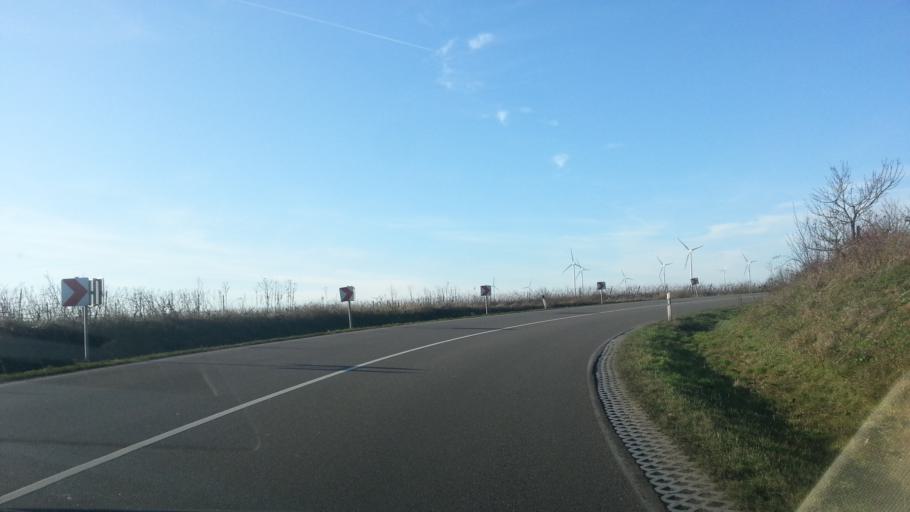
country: DE
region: Rheinland-Pfalz
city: Monsheim
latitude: 49.6287
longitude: 8.1992
